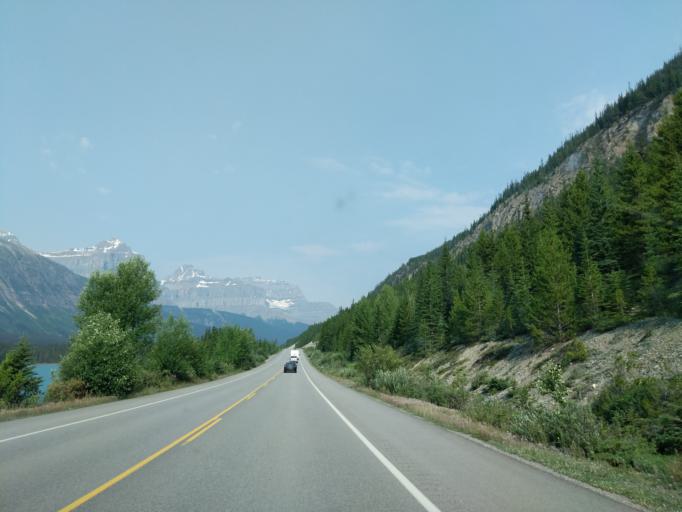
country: CA
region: Alberta
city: Lake Louise
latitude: 51.8531
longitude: -116.6362
